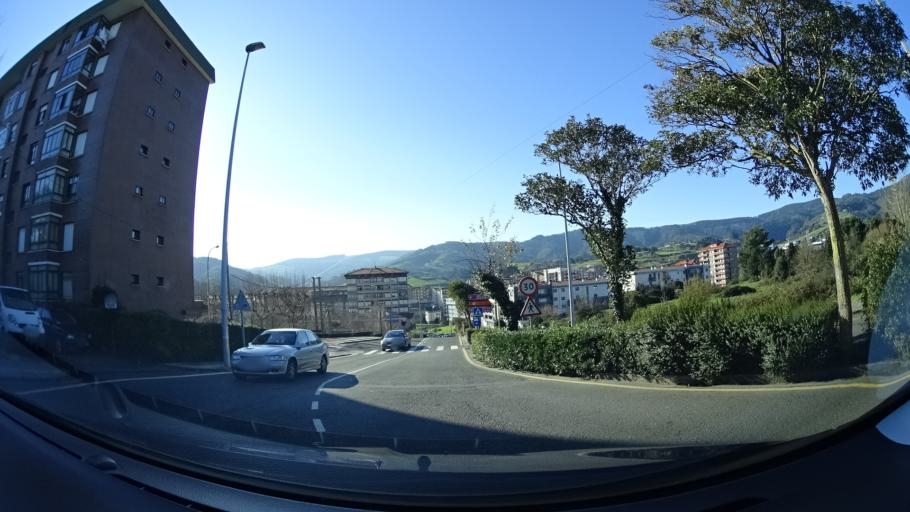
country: ES
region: Basque Country
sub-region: Bizkaia
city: Bermeo
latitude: 43.4230
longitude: -2.7279
